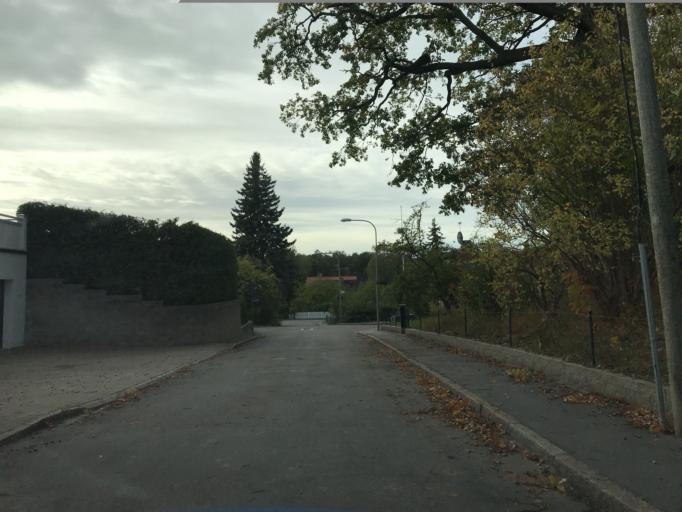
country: SE
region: Stockholm
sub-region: Huddinge Kommun
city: Segeltorp
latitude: 59.2766
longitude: 17.9586
